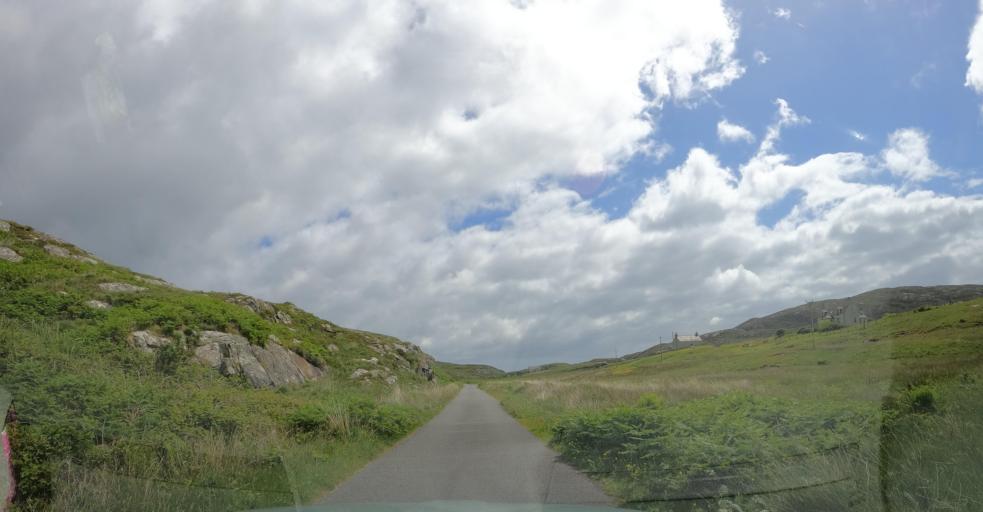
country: GB
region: Scotland
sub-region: Eilean Siar
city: Isle of South Uist
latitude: 57.0701
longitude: -7.2953
